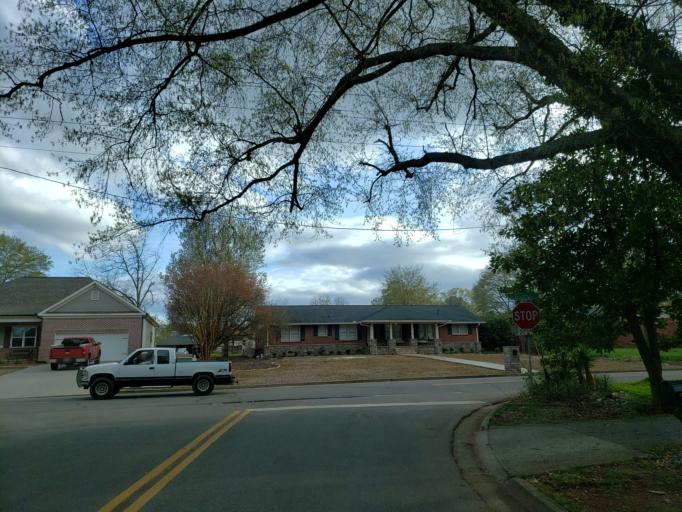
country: US
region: Georgia
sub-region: Bartow County
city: Cartersville
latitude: 34.1579
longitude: -84.8007
